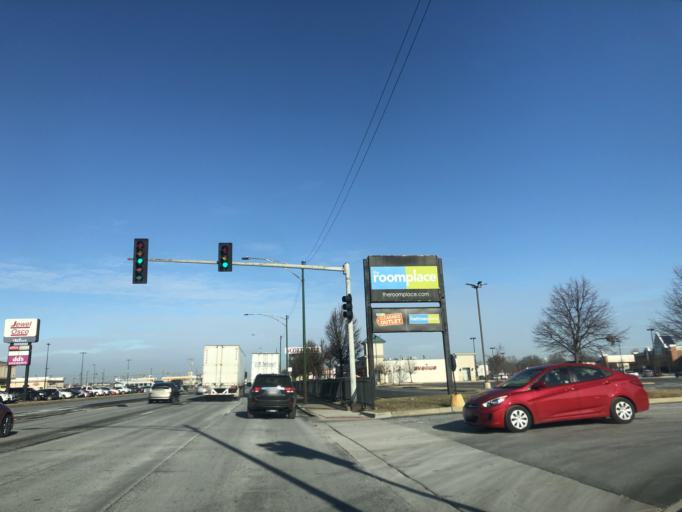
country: US
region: Illinois
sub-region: Cook County
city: Hometown
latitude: 41.7461
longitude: -87.7411
